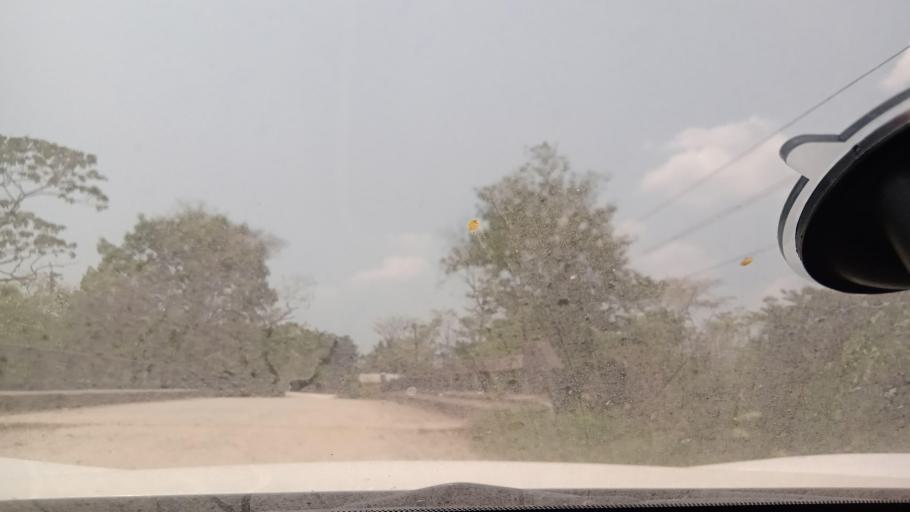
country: MX
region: Chiapas
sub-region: Tecpatan
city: Raudales Malpaso
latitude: 17.4583
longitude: -93.7988
